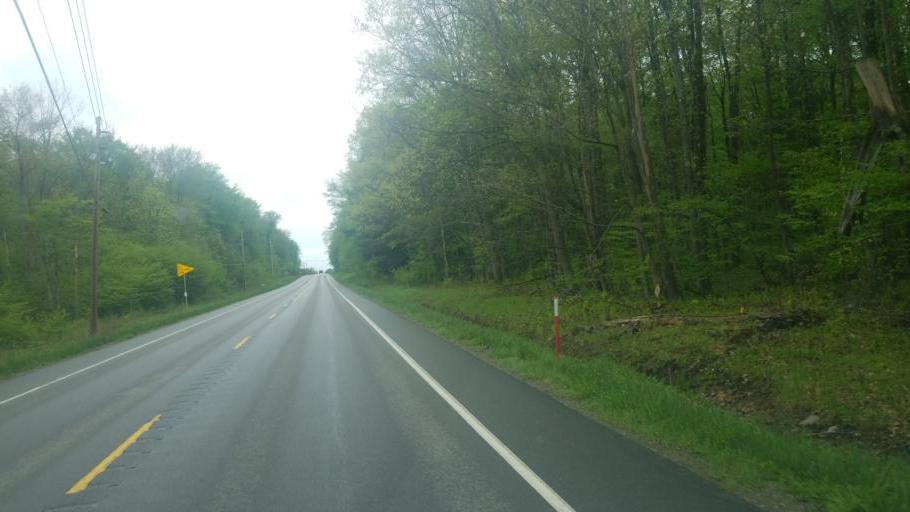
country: US
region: Pennsylvania
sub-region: Forest County
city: Marienville
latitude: 41.4883
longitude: -79.0980
